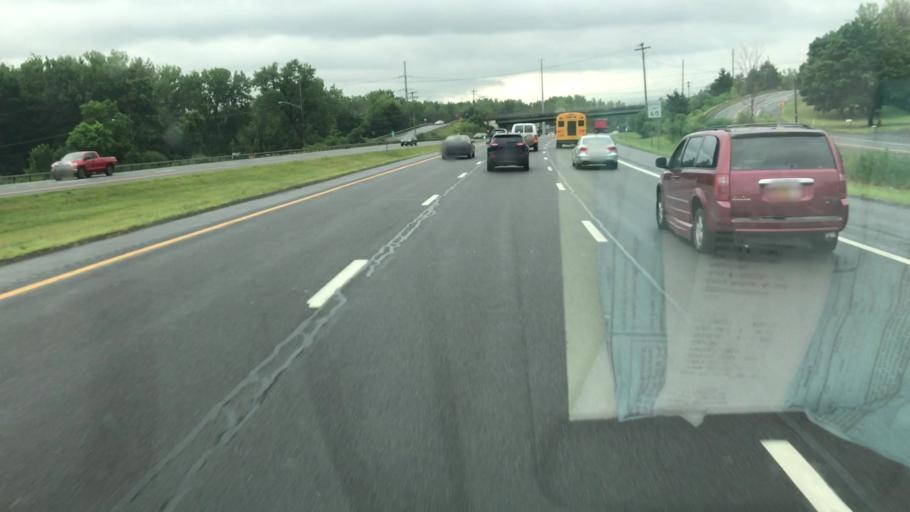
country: US
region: New York
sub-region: Onondaga County
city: East Syracuse
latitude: 43.0460
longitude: -76.0513
